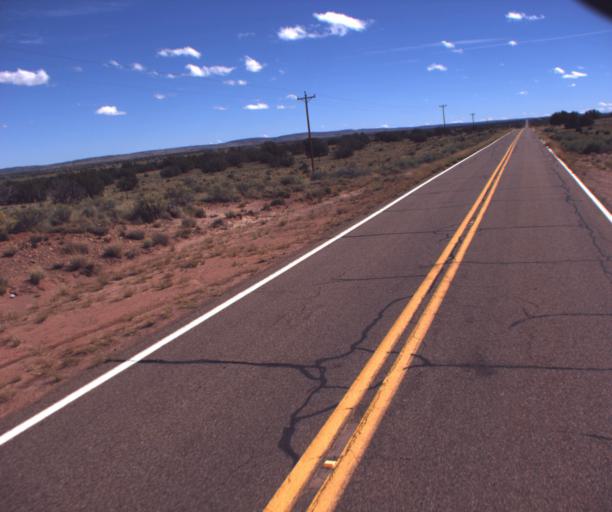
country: US
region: Arizona
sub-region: Apache County
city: Saint Johns
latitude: 34.6162
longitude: -109.6612
